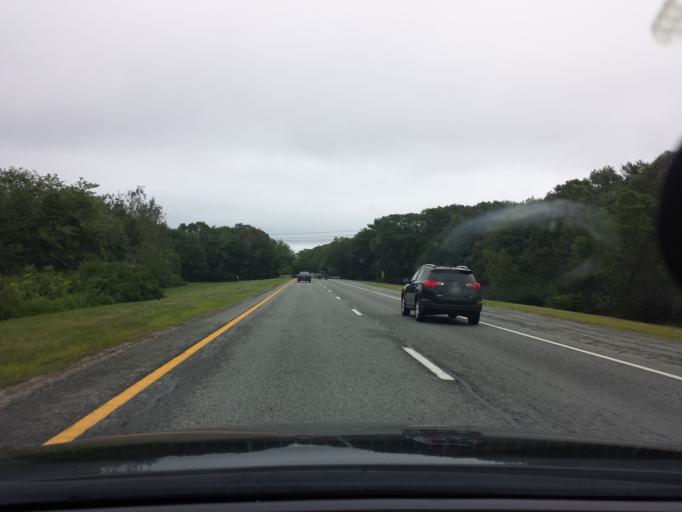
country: US
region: Rhode Island
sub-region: Kent County
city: East Greenwich
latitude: 41.6667
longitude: -71.4933
